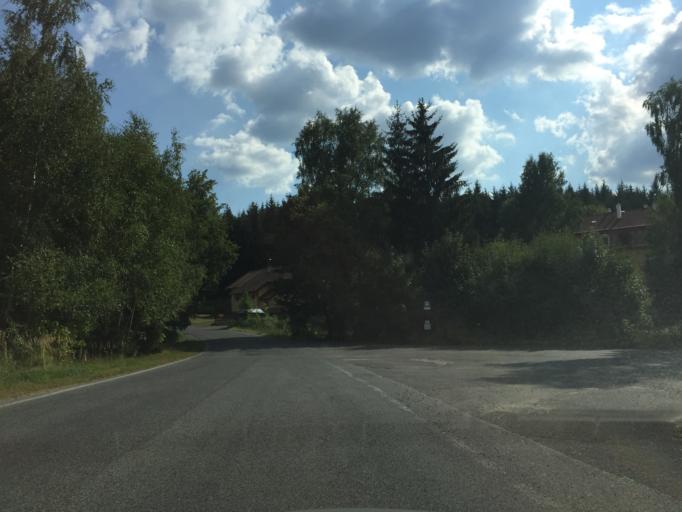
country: CZ
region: Liberecky
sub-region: Okres Jablonec nad Nisou
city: Jablonec nad Nisou
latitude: 50.7165
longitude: 15.1878
